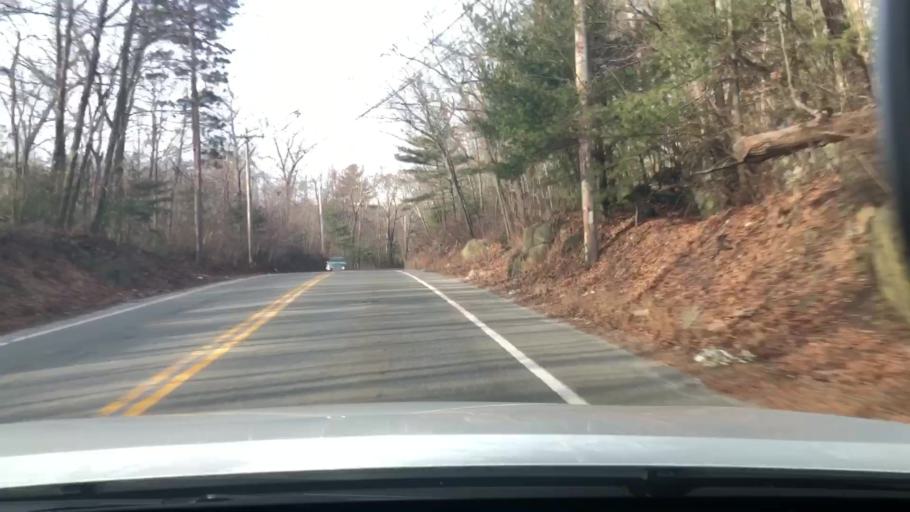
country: US
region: Massachusetts
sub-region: Worcester County
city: Upton
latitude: 42.1663
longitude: -71.5929
